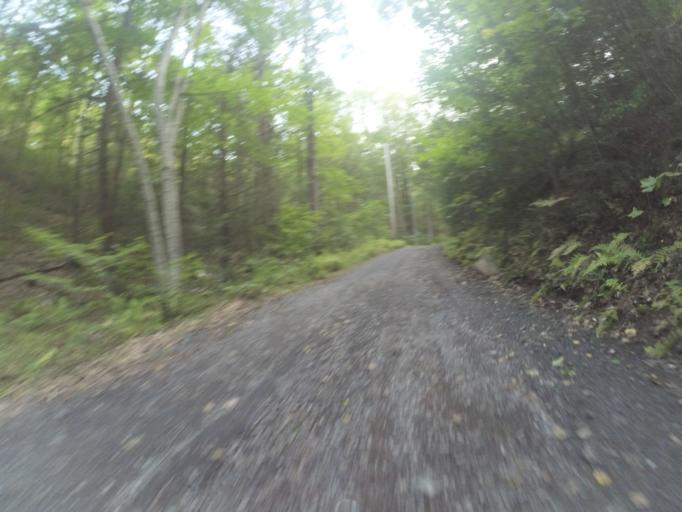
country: US
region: Pennsylvania
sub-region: Mifflin County
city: Milroy
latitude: 40.8509
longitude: -77.4636
